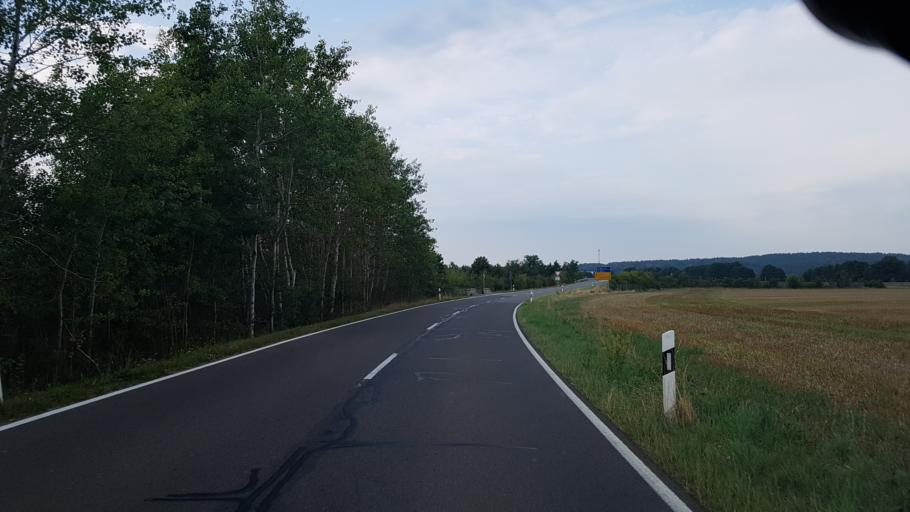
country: DE
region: Brandenburg
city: Ortrand
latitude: 51.3873
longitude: 13.7475
